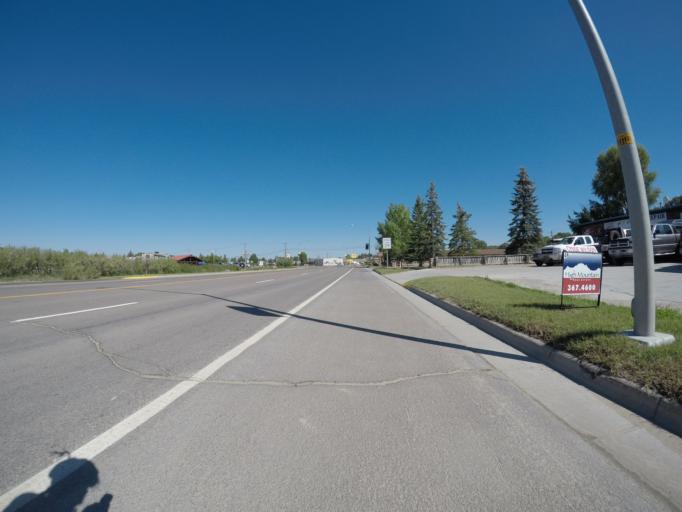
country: US
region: Wyoming
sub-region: Sublette County
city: Pinedale
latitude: 42.8647
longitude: -109.8540
